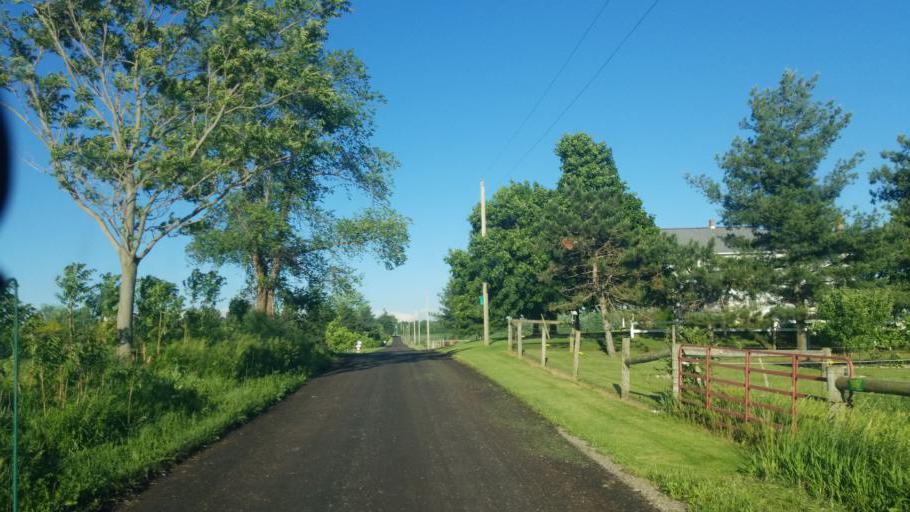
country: US
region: Indiana
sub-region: Marshall County
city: Bremen
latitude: 41.4192
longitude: -86.0817
